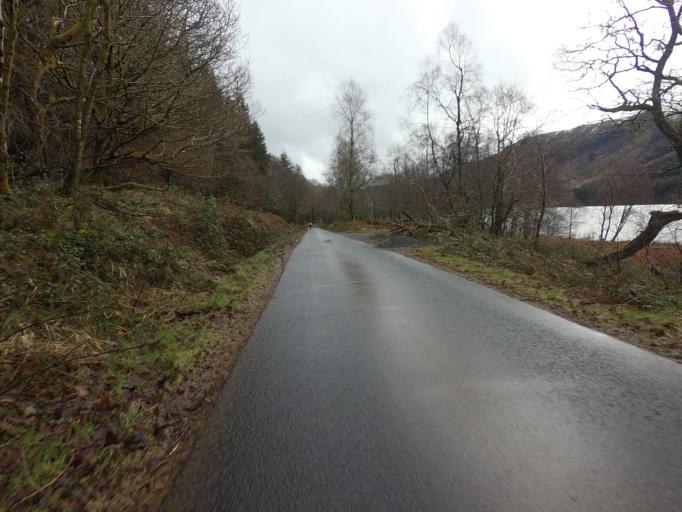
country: GB
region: Scotland
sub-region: West Dunbartonshire
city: Balloch
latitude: 56.2244
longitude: -4.5524
